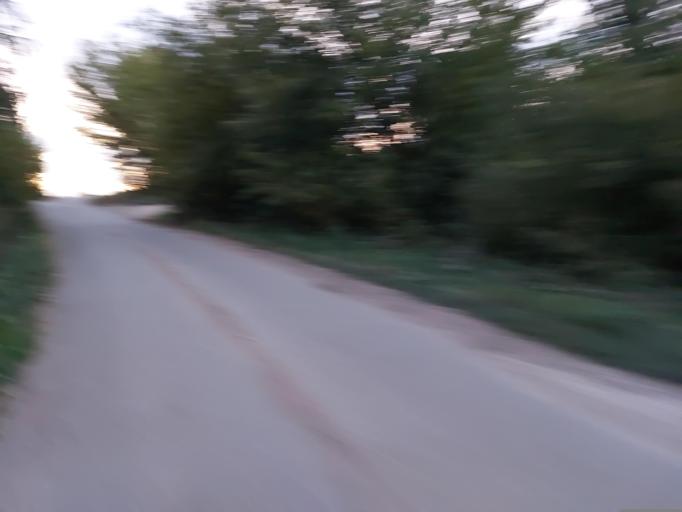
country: RU
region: Lipetsk
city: Dolgorukovo
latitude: 52.3792
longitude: 38.0466
